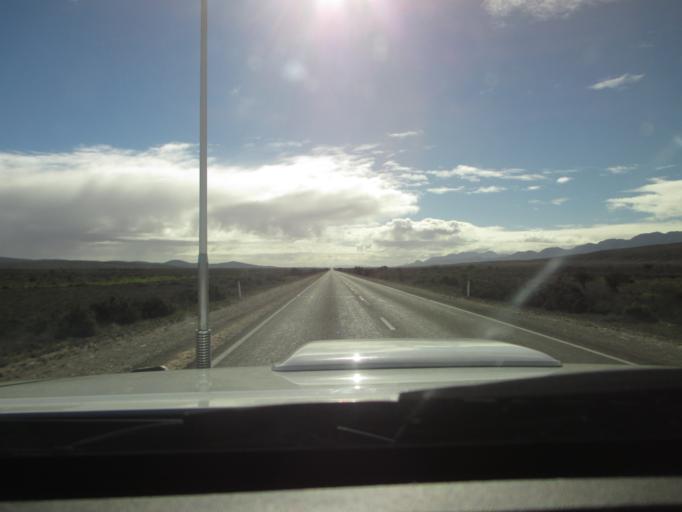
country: AU
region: South Australia
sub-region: Flinders Ranges
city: Quorn
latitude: -31.7278
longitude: 138.3444
